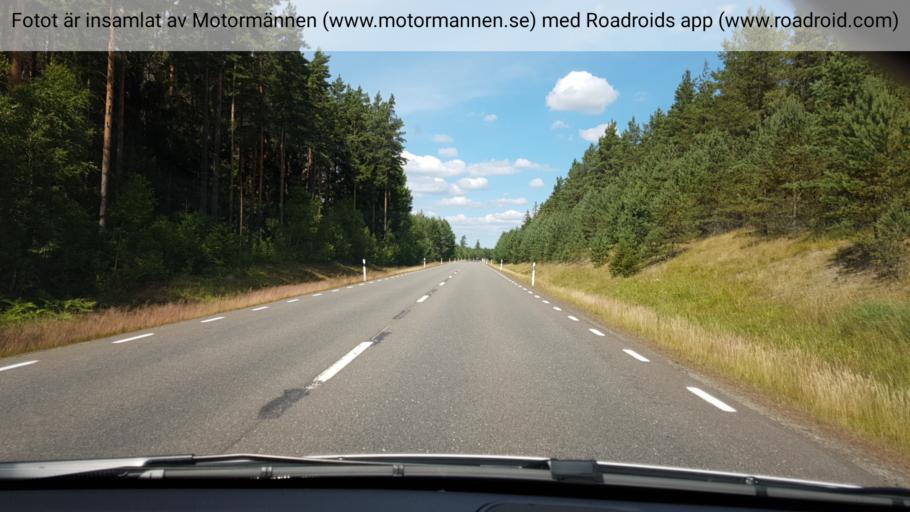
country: SE
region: Vaestra Goetaland
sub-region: Tibro Kommun
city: Tibro
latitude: 58.5112
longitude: 14.1650
